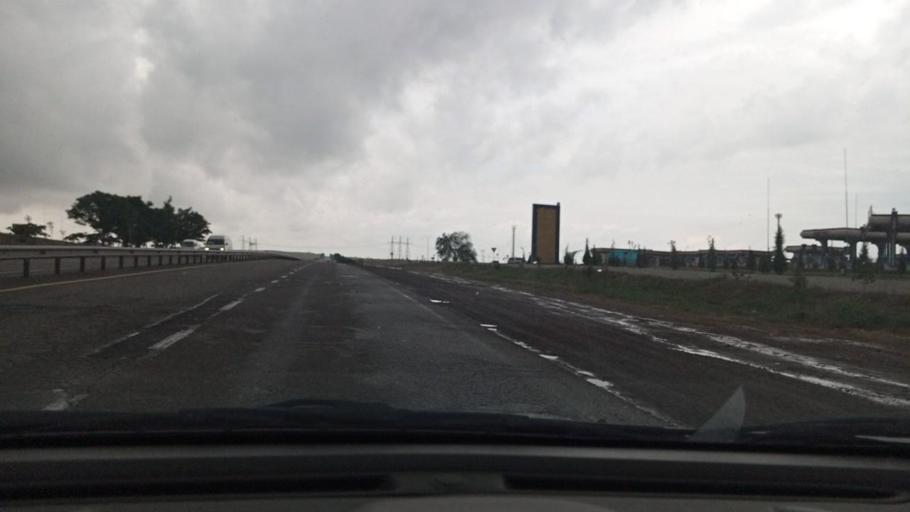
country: UZ
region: Toshkent
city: Ohangaron
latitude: 40.9405
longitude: 69.5826
